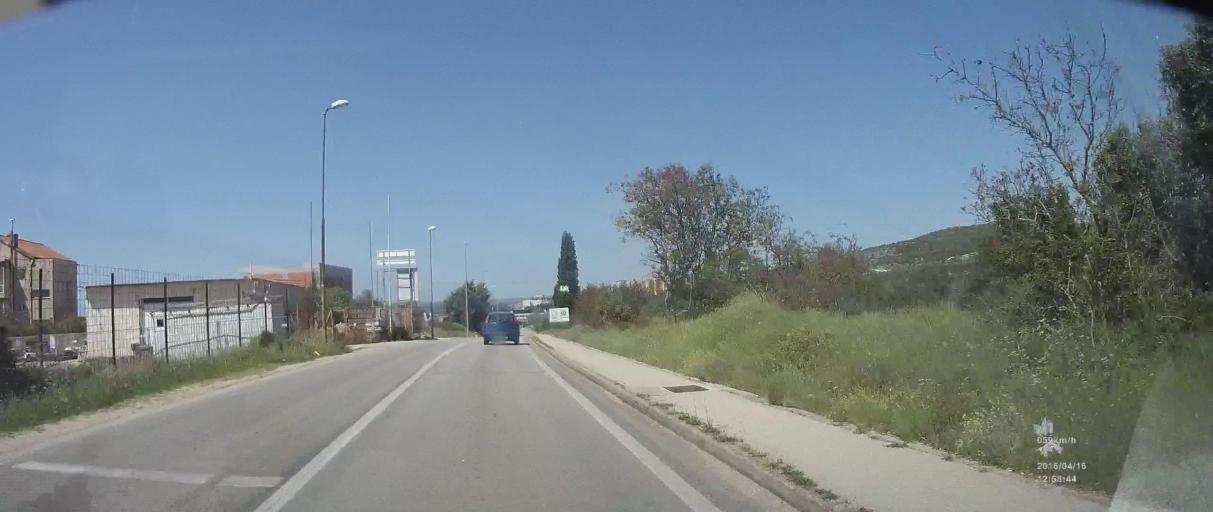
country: HR
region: Sibensko-Kniniska
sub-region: Grad Sibenik
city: Sibenik
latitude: 43.7106
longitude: 15.9204
